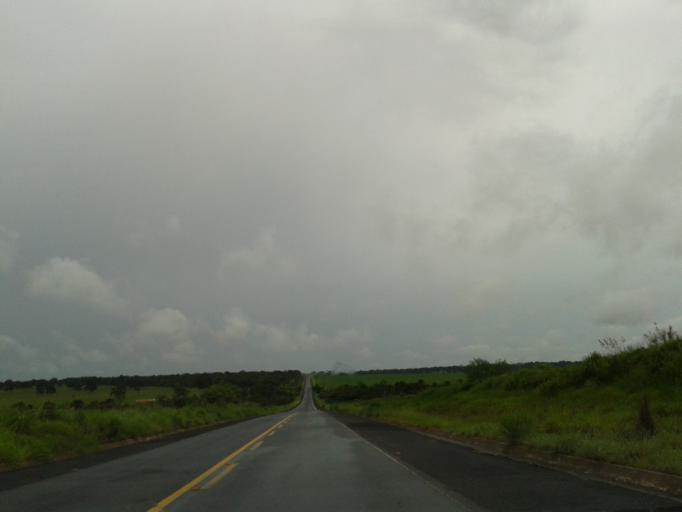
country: BR
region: Minas Gerais
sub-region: Santa Vitoria
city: Santa Vitoria
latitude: -19.1514
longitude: -50.1499
